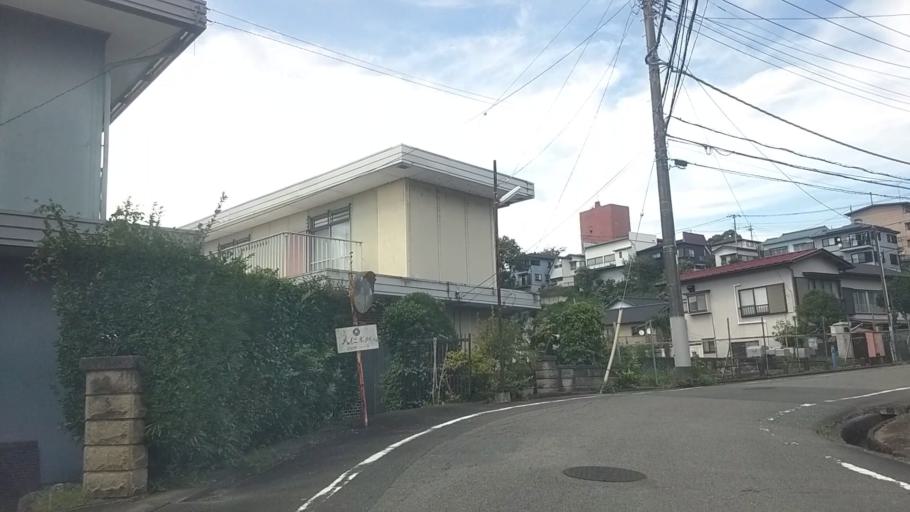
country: JP
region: Shizuoka
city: Mishima
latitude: 34.9944
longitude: 138.9414
